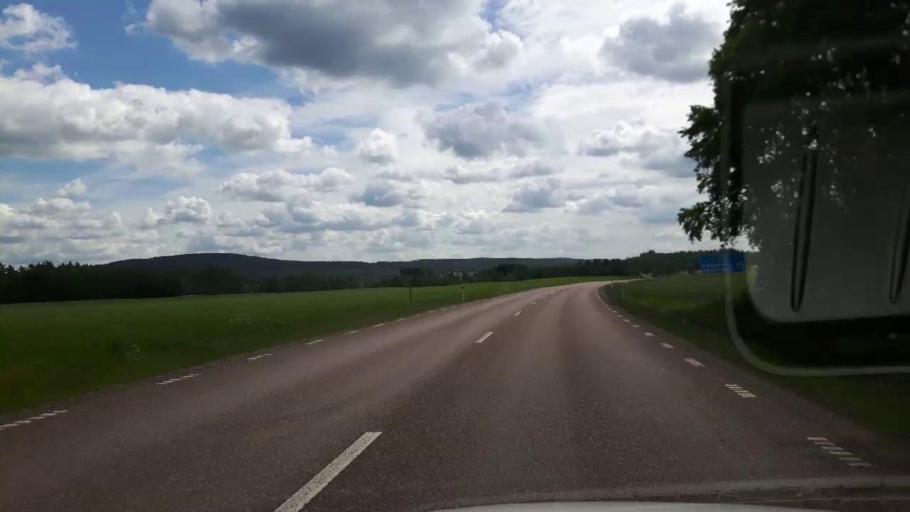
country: SE
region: Dalarna
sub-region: Hedemora Kommun
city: Langshyttan
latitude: 60.3889
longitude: 15.9021
